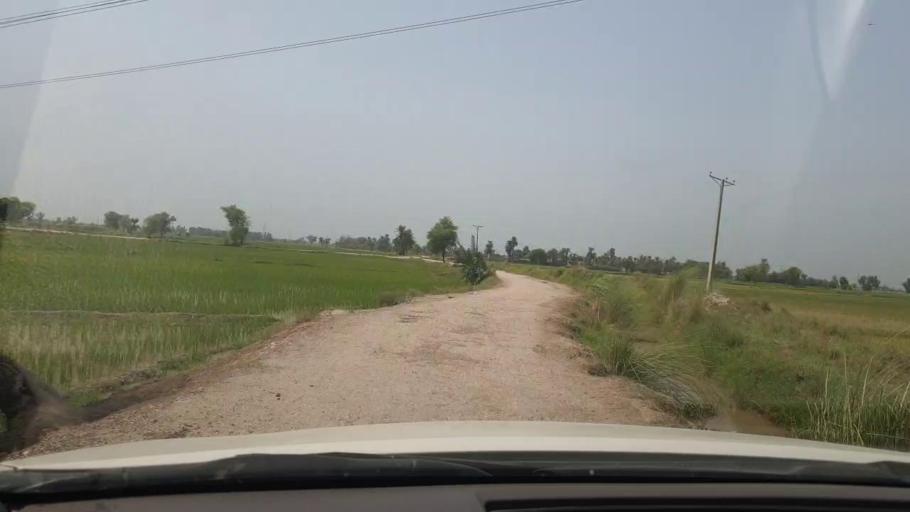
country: PK
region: Sindh
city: Shikarpur
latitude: 28.0117
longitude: 68.6483
